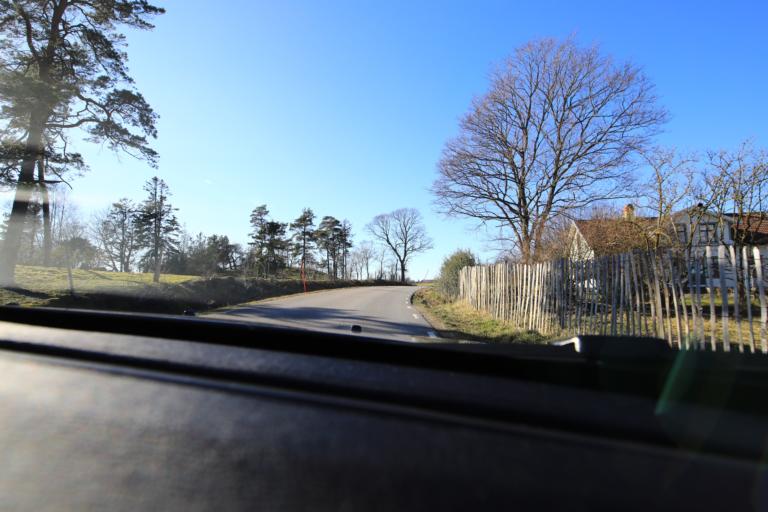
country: SE
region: Halland
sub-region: Varbergs Kommun
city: Tvaaker
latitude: 57.0671
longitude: 12.3804
